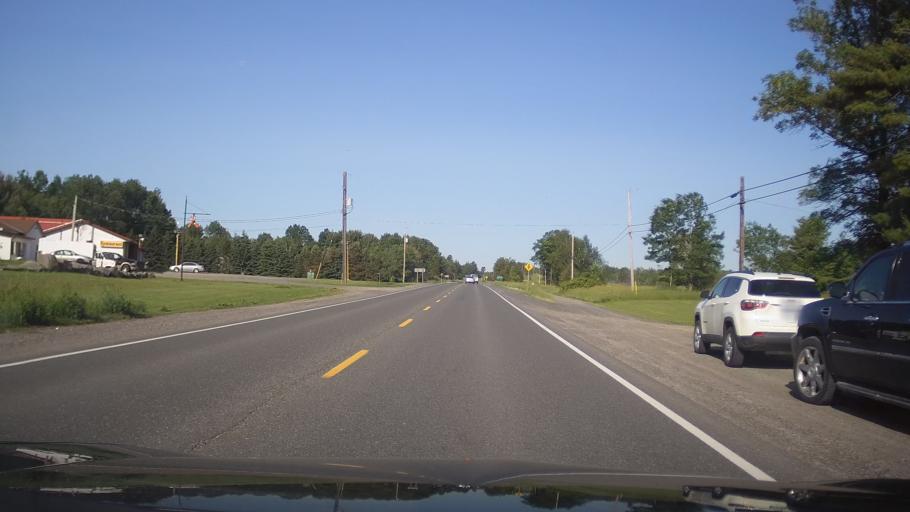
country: CA
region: Ontario
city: Quinte West
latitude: 44.4547
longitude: -77.7718
